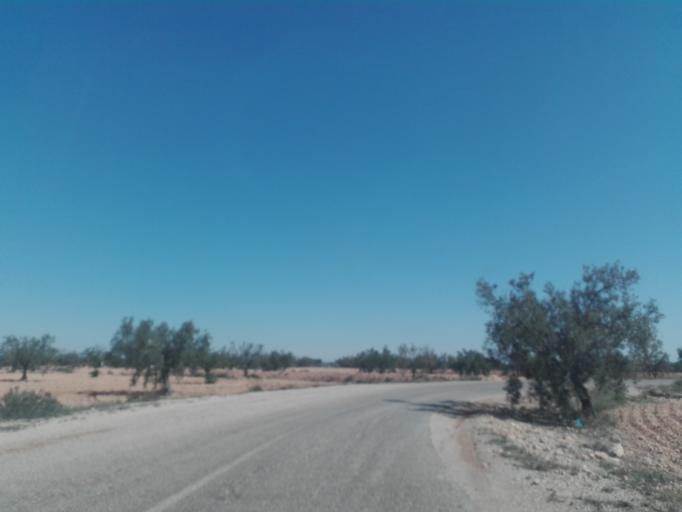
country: TN
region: Safaqis
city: Bi'r `Ali Bin Khalifah
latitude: 34.8347
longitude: 10.2728
